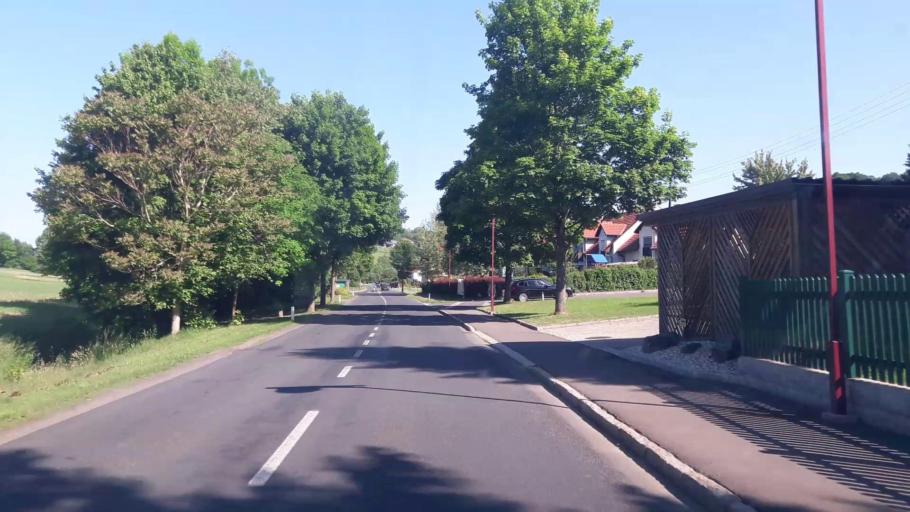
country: AT
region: Styria
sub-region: Politischer Bezirk Suedoststeiermark
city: Unterlamm
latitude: 46.9814
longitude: 16.0562
